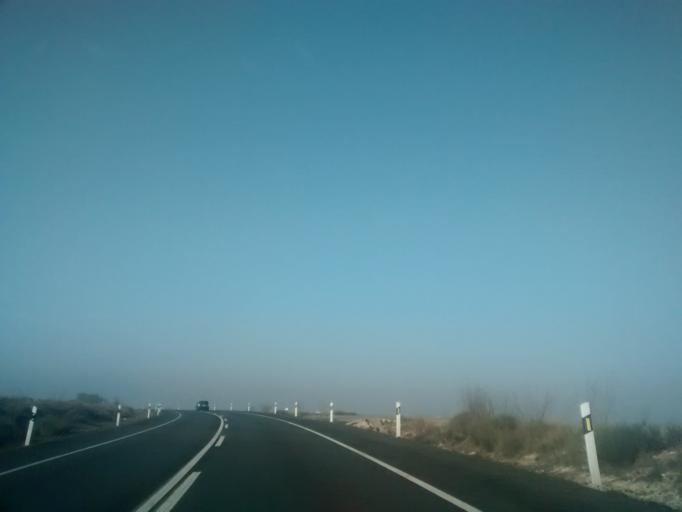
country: ES
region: Aragon
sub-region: Provincia de Huesca
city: Candasnos
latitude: 41.5180
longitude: 0.1409
